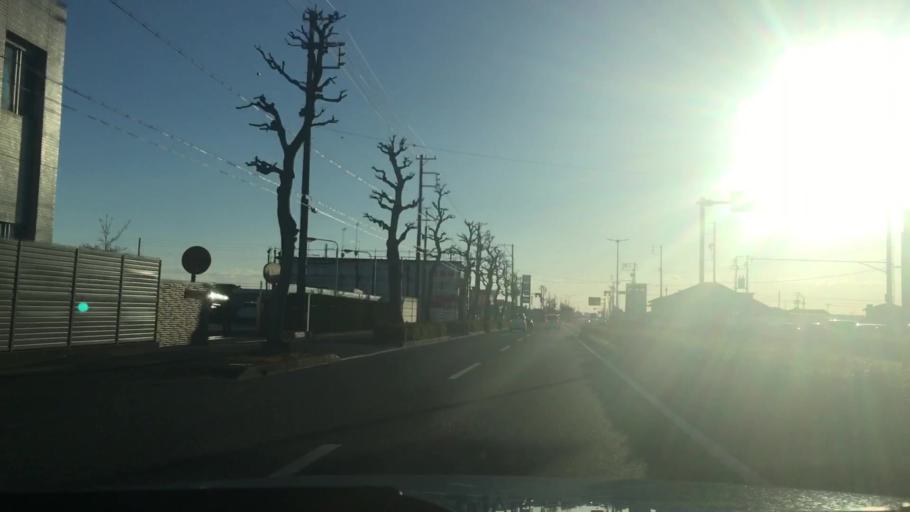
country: JP
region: Shizuoka
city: Hamamatsu
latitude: 34.7582
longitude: 137.6791
